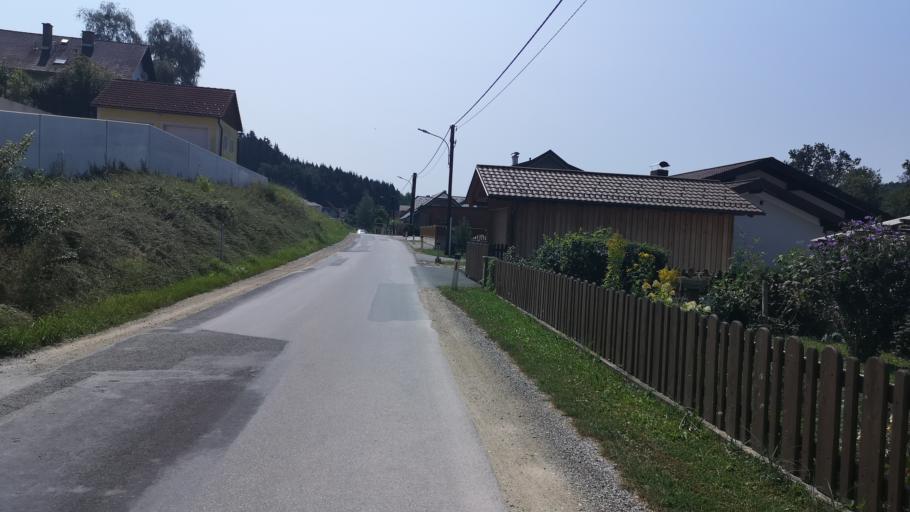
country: AT
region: Styria
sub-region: Politischer Bezirk Deutschlandsberg
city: Sankt Josef (Weststeiermark)
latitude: 46.8967
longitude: 15.3645
